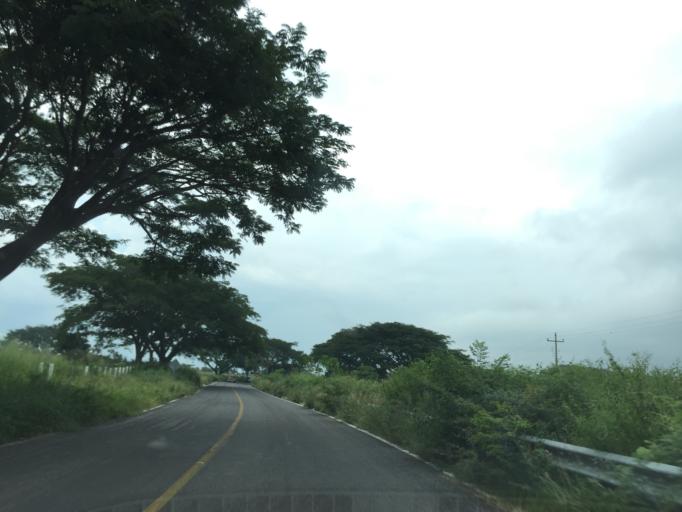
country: MX
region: Colima
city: Comala
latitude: 19.3606
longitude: -103.7943
